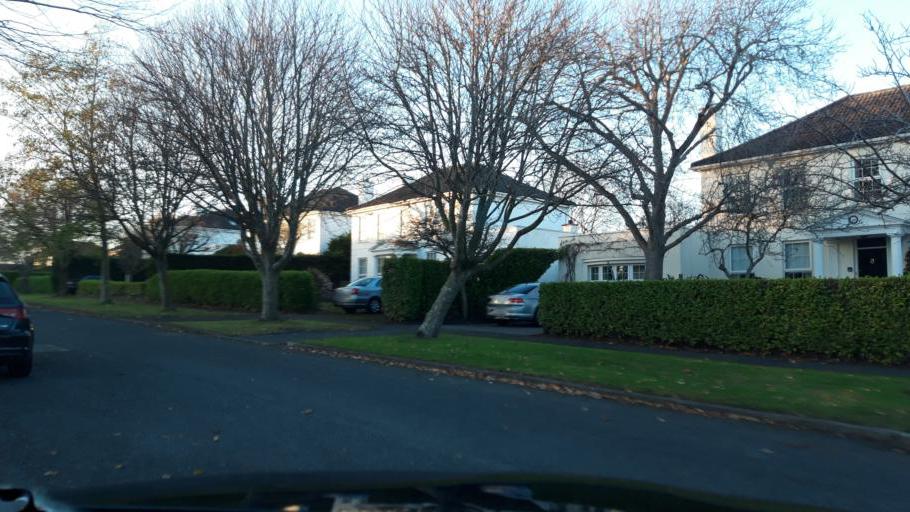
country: IE
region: Leinster
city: Castleknock
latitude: 53.3691
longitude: -6.3564
